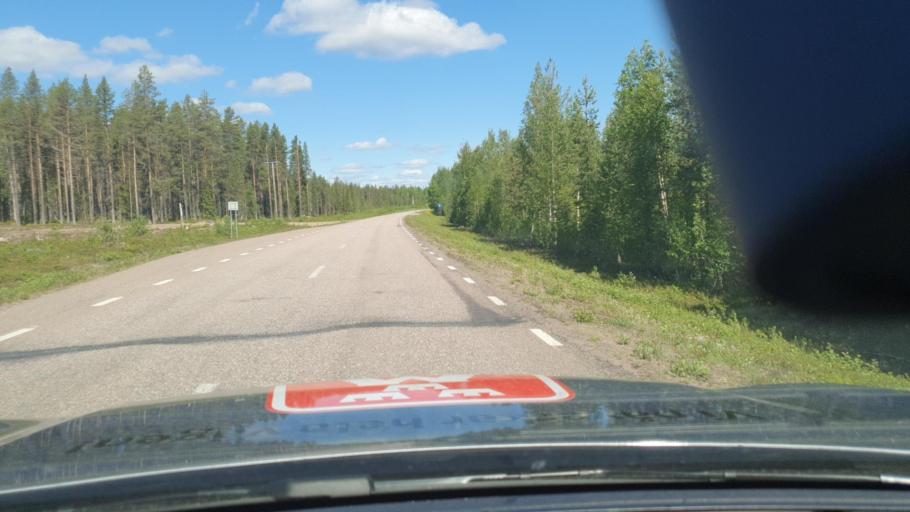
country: SE
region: Norrbotten
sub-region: Overkalix Kommun
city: OEverkalix
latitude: 67.0352
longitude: 22.5040
